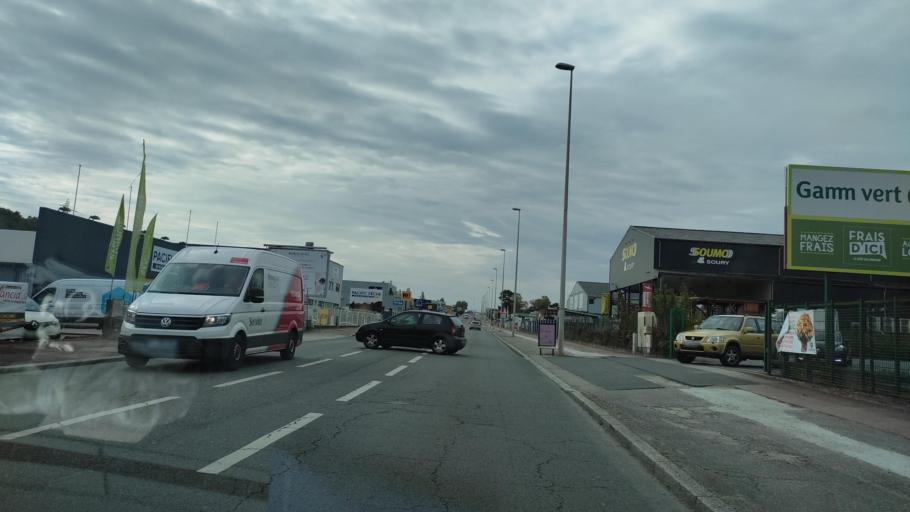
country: FR
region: Limousin
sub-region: Departement de la Haute-Vienne
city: Couzeix
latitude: 45.8766
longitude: 1.2731
